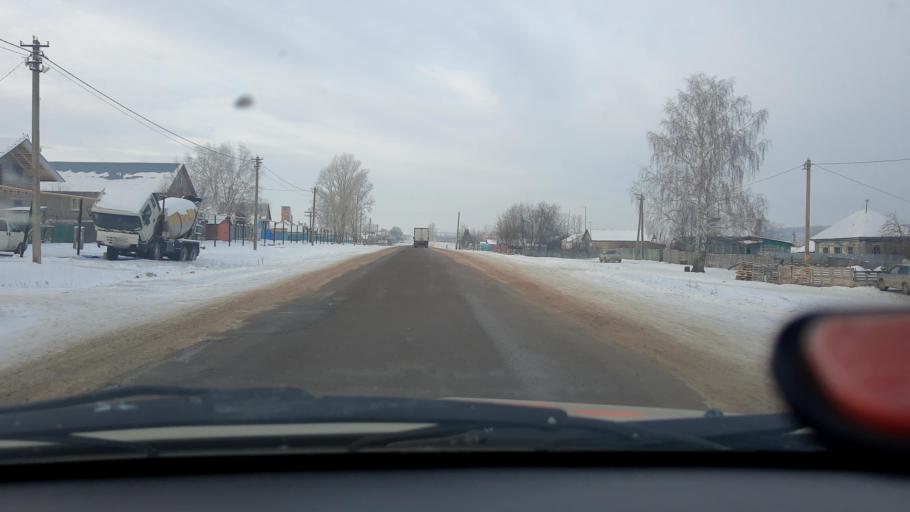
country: RU
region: Bashkortostan
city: Avdon
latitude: 54.3602
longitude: 55.8411
